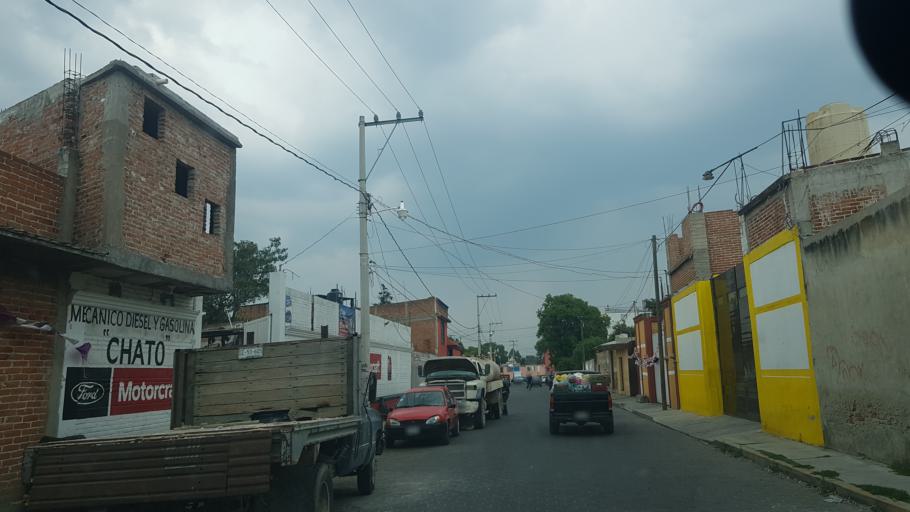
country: MX
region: Puebla
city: Huejotzingo
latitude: 19.1664
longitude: -98.4105
